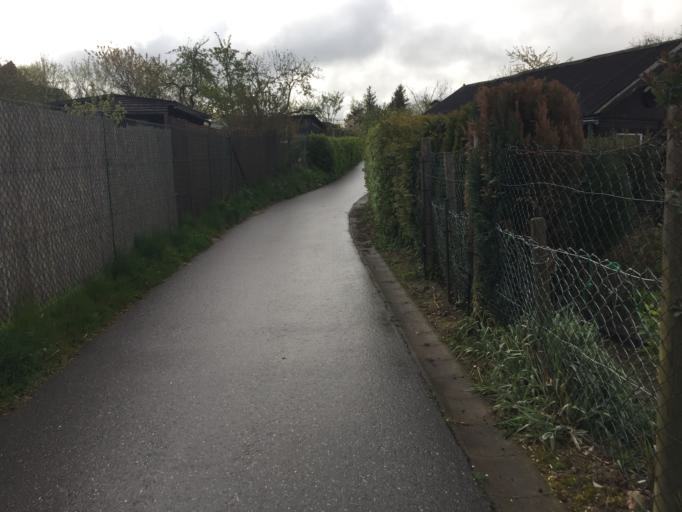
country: DE
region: Schleswig-Holstein
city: Flensburg
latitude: 54.7786
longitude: 9.4528
